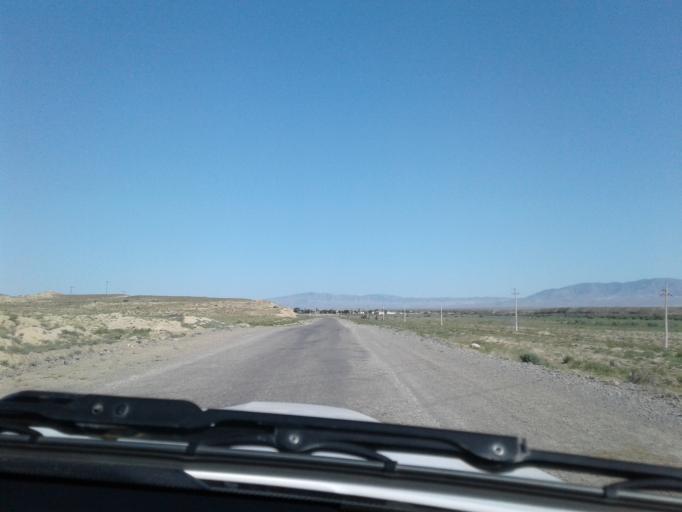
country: TM
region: Balkan
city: Serdar
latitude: 38.7153
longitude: 56.3248
